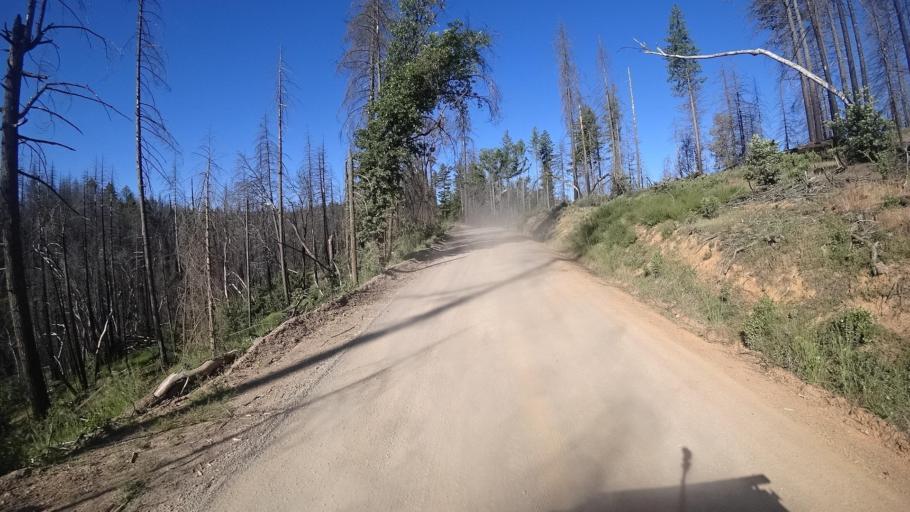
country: US
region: California
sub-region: Lake County
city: Upper Lake
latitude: 39.3918
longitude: -122.9766
